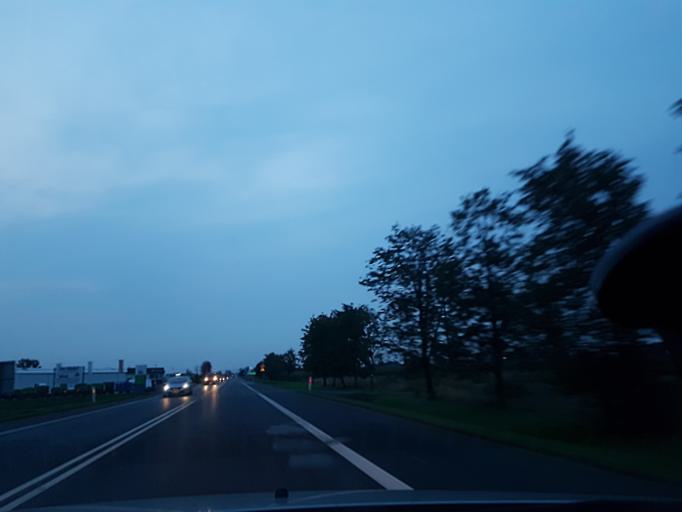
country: PL
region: Lodz Voivodeship
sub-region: Powiat kutnowski
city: Krzyzanow
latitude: 52.2222
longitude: 19.4396
